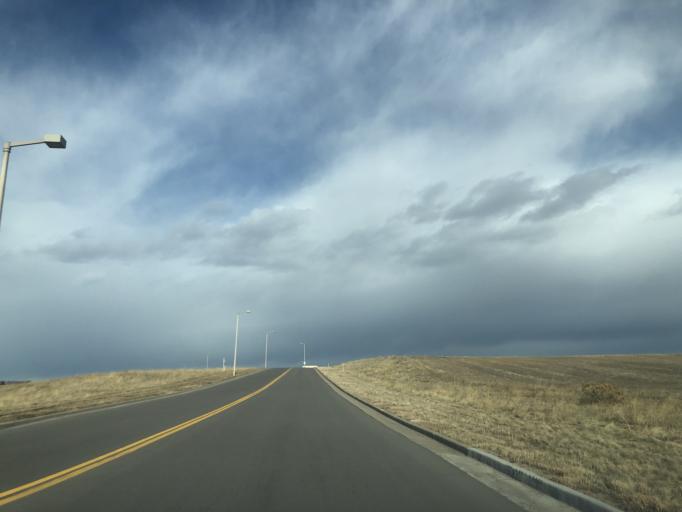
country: US
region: Colorado
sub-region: Douglas County
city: Meridian
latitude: 39.5549
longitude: -104.8569
